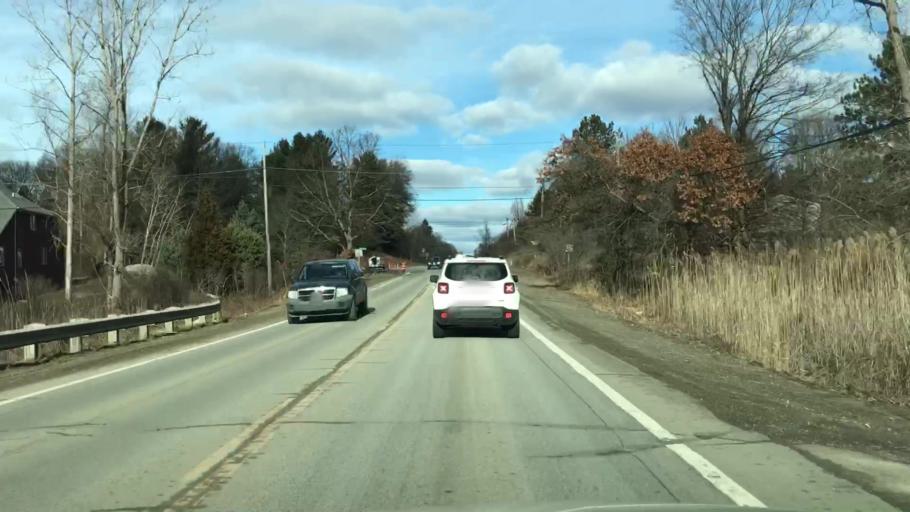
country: US
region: Michigan
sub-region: Oakland County
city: Lake Orion
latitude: 42.7473
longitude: -83.1971
